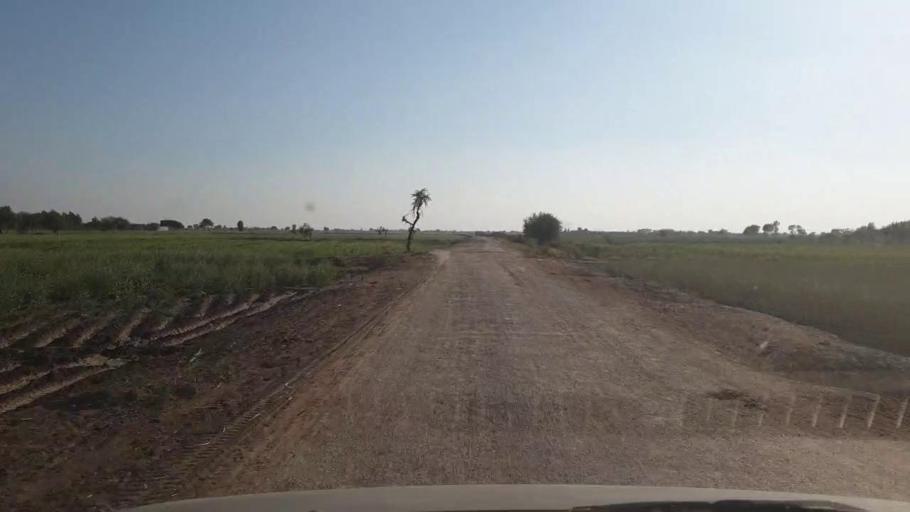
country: PK
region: Sindh
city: Mirwah Gorchani
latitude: 25.3656
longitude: 69.0965
